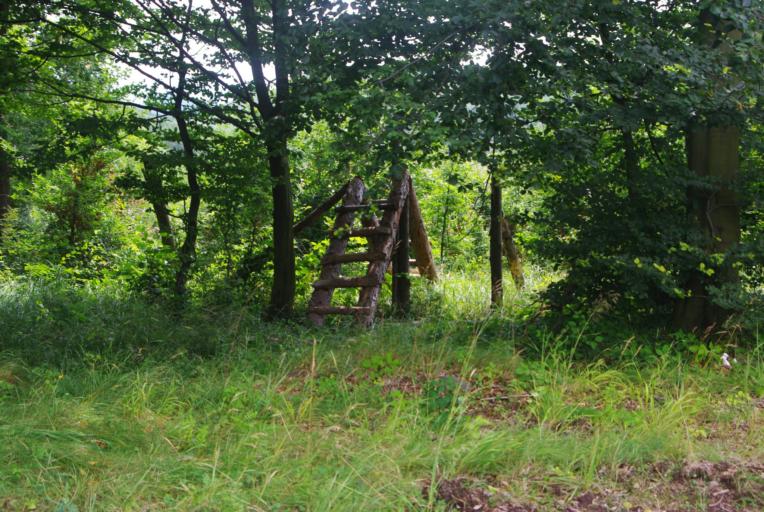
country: HU
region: Borsod-Abauj-Zemplen
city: Gonc
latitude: 48.4120
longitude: 21.3785
